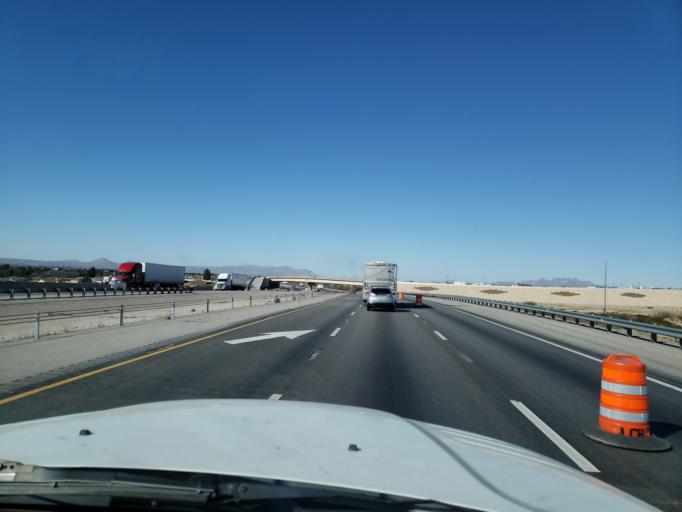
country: US
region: New Mexico
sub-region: Dona Ana County
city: University Park
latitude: 32.2595
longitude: -106.7312
